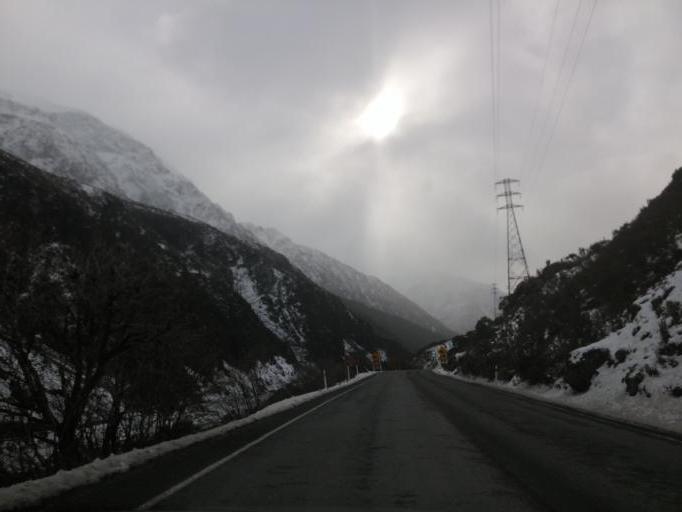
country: NZ
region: West Coast
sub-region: Grey District
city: Greymouth
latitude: -42.8931
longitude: 171.5580
